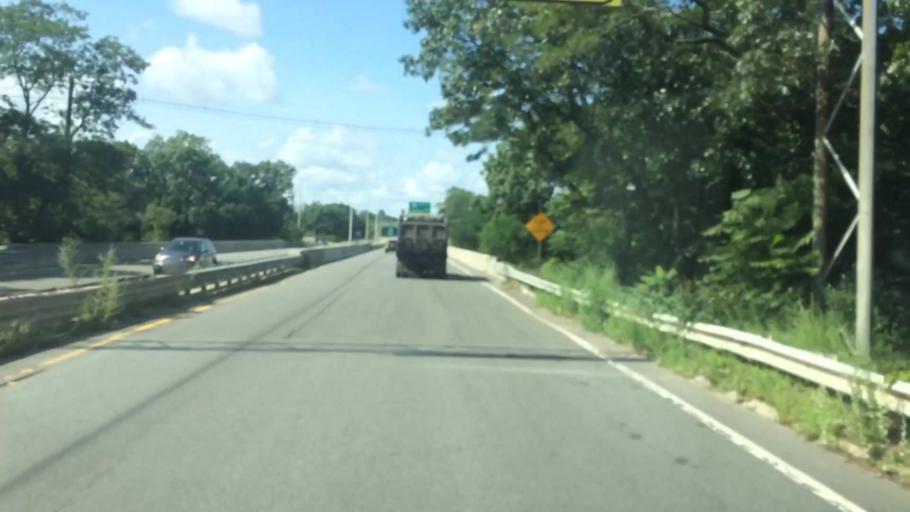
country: US
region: Massachusetts
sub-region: Essex County
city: South Peabody
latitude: 42.5188
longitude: -70.9931
